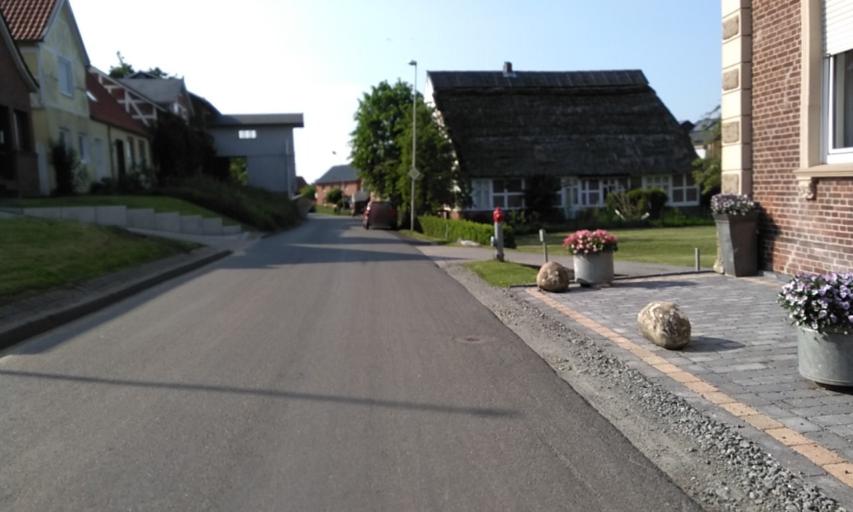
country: DE
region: Lower Saxony
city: Jork
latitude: 53.5120
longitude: 9.7313
